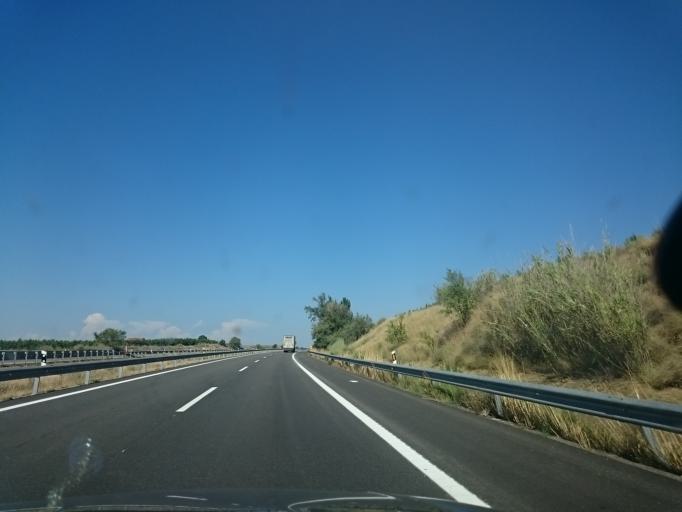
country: ES
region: Catalonia
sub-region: Provincia de Lleida
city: Seros
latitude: 41.5058
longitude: 0.4104
